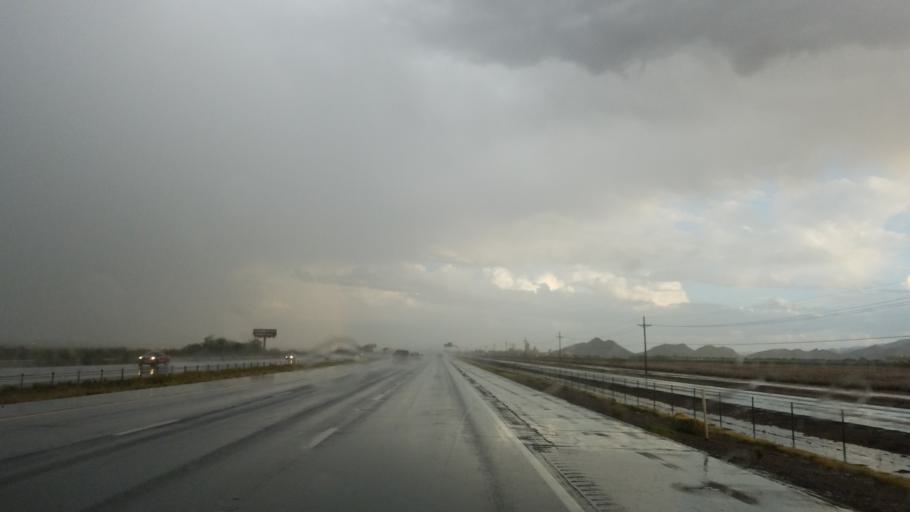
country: US
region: Arizona
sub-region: Pima County
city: Marana
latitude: 32.4351
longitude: -111.1788
